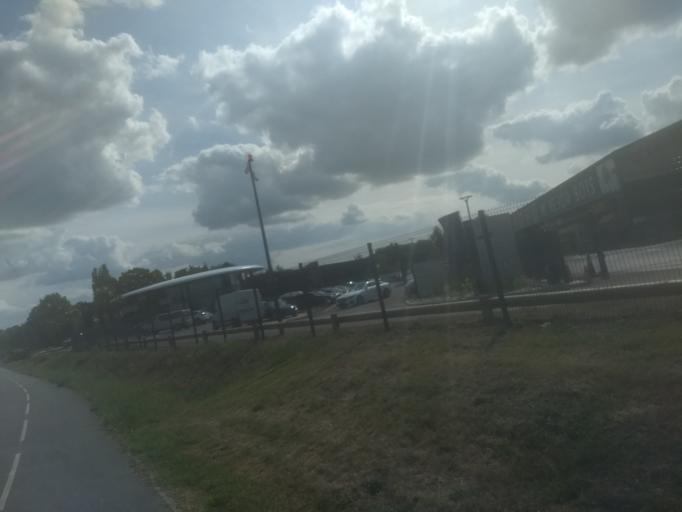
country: FR
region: Nord-Pas-de-Calais
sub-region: Departement du Pas-de-Calais
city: Beaurains
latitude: 50.2637
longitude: 2.7955
